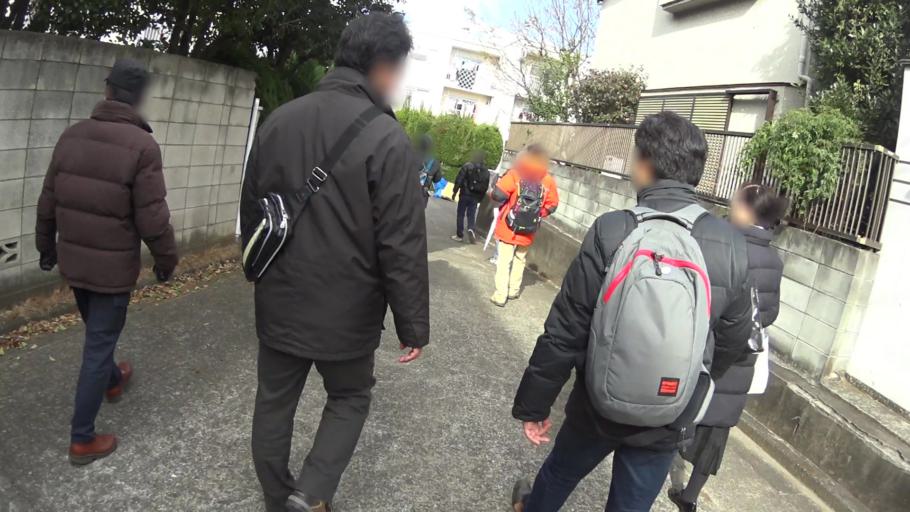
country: JP
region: Tokyo
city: Tokyo
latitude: 35.6748
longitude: 139.6805
